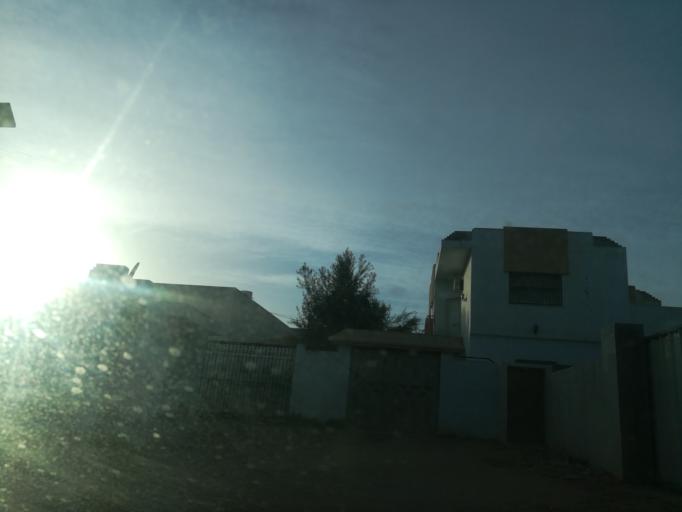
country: TN
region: Safaqis
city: Al Qarmadah
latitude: 34.8156
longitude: 10.7530
